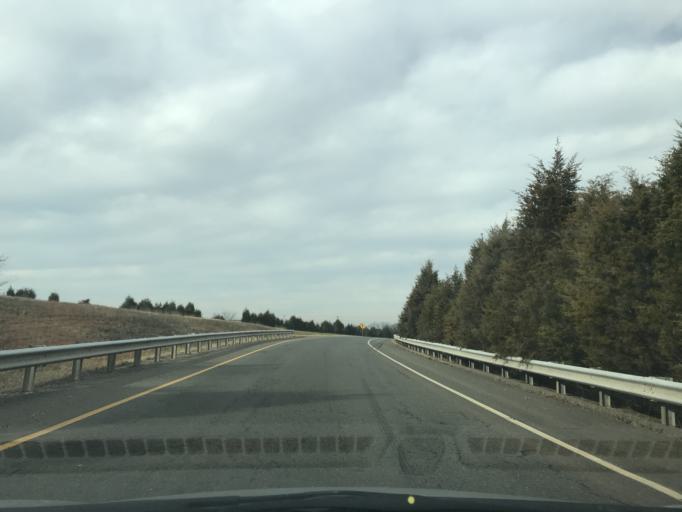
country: US
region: Virginia
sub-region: Prince William County
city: Bull Run
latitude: 38.7440
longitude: -77.5189
